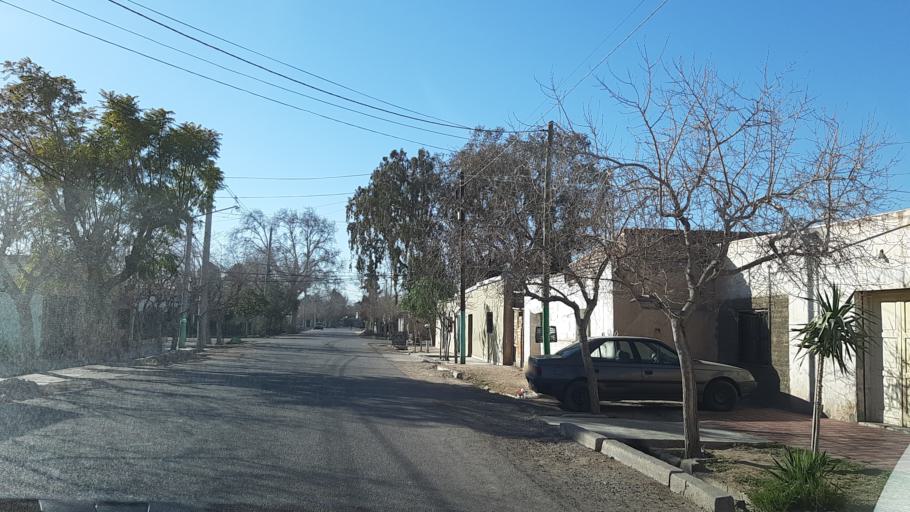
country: AR
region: San Juan
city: San Juan
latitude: -31.5378
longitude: -68.5707
